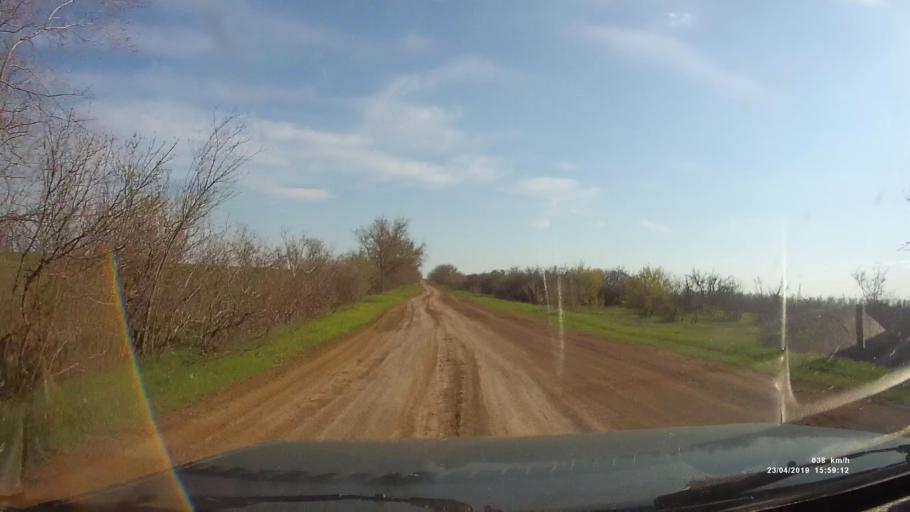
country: RU
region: Rostov
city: Remontnoye
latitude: 46.5184
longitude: 43.1096
